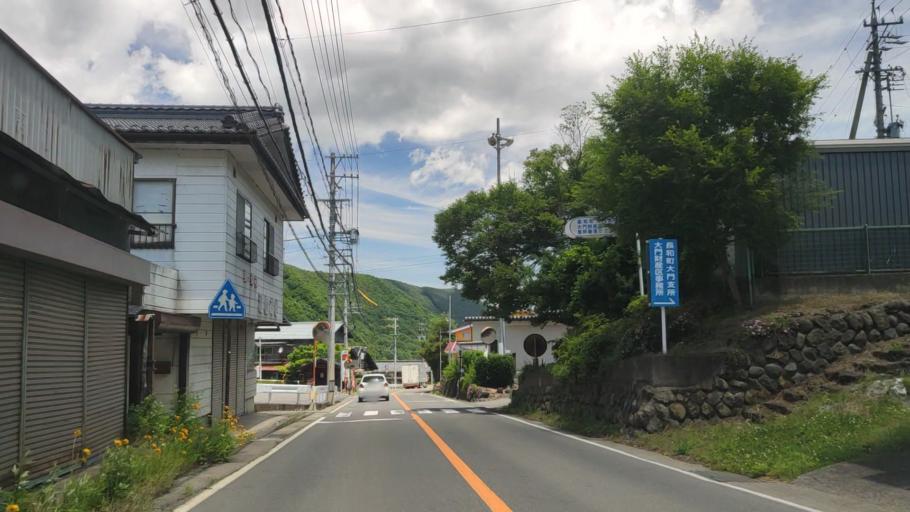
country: JP
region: Nagano
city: Kamimaruko
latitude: 36.2210
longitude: 138.2506
